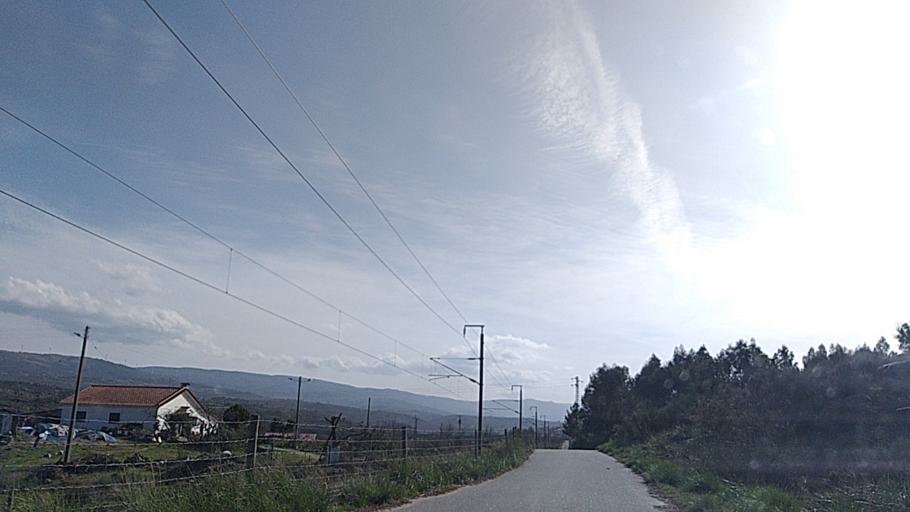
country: PT
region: Guarda
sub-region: Celorico da Beira
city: Celorico da Beira
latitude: 40.6405
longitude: -7.4313
